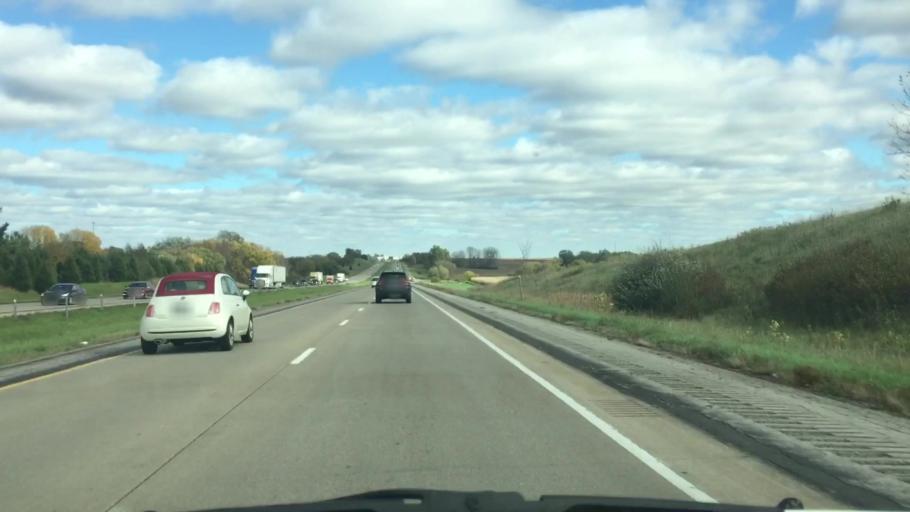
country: US
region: Iowa
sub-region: Cedar County
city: West Branch
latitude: 41.6672
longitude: -91.4156
